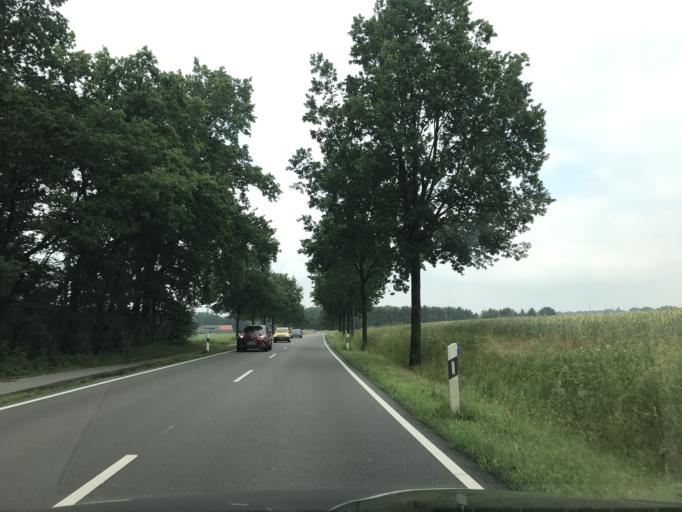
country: DE
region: Lower Saxony
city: Kirchseelte
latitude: 52.9585
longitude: 8.7146
